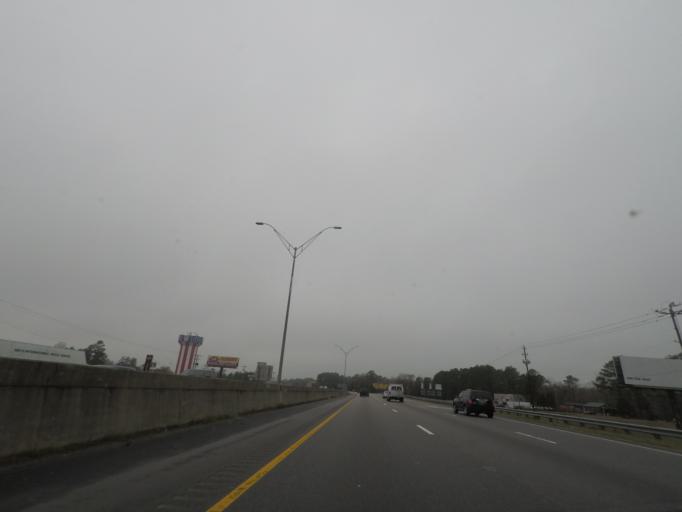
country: US
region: North Carolina
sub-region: Robeson County
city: Lumberton
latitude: 34.6221
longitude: -79.0566
